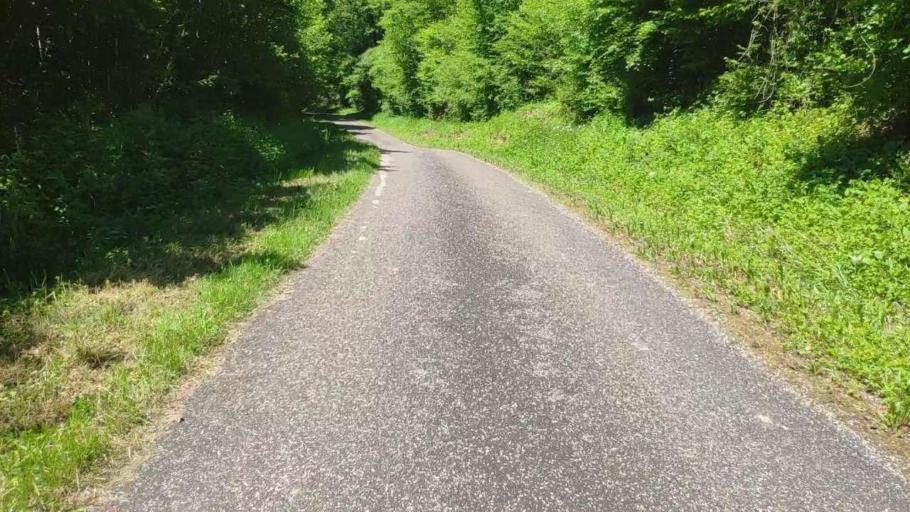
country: FR
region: Franche-Comte
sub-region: Departement du Jura
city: Perrigny
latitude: 46.7339
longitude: 5.6531
